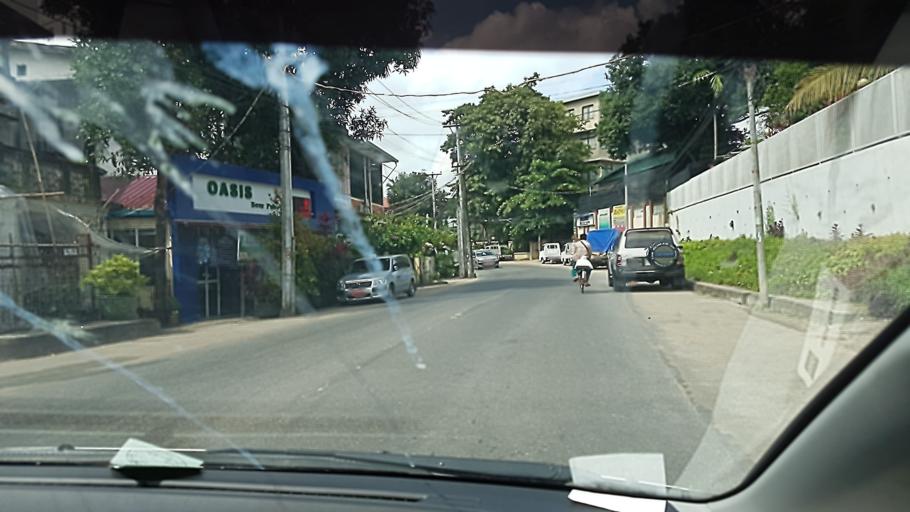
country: MM
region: Yangon
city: Yangon
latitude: 16.8047
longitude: 96.1719
